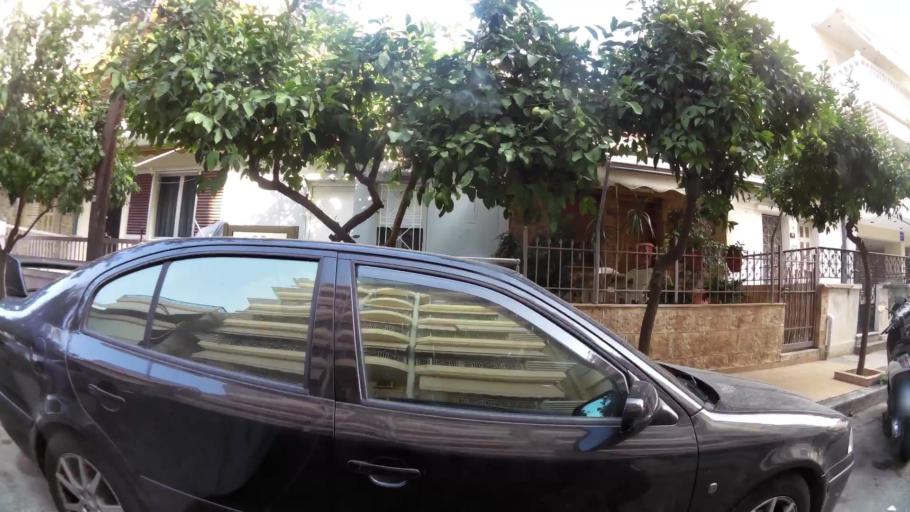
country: GR
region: Attica
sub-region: Nomos Piraios
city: Keratsini
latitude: 37.9668
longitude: 23.6221
